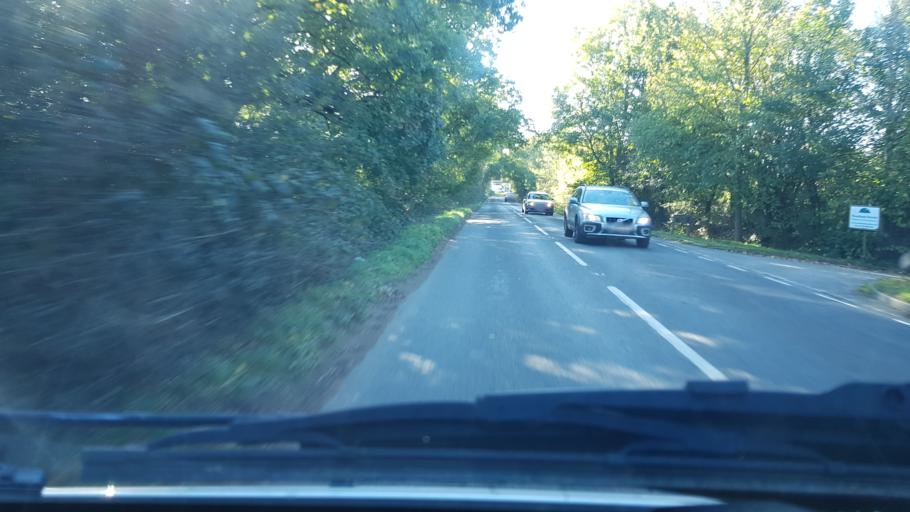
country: GB
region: England
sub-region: Surrey
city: Cranleigh
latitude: 51.1678
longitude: -0.5111
